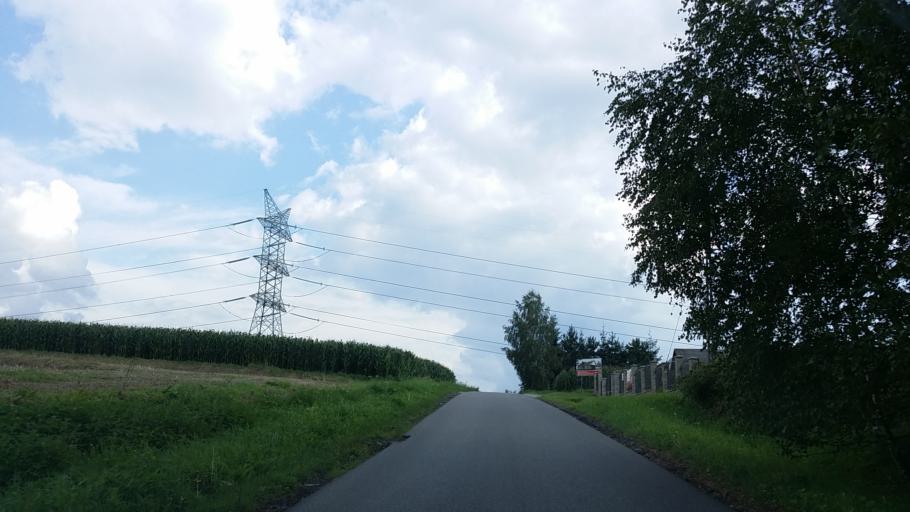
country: PL
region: Lesser Poland Voivodeship
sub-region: Powiat wadowicki
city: Bachowice
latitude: 49.9885
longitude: 19.4760
